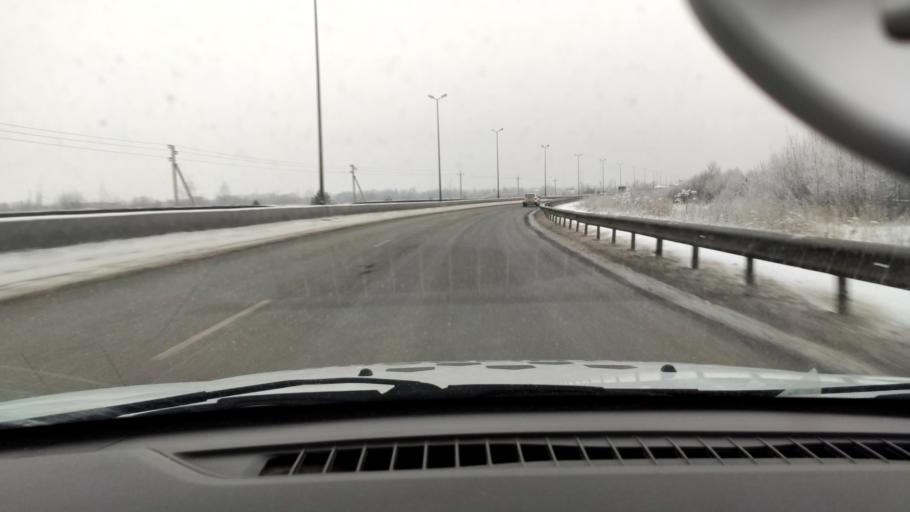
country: RU
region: Perm
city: Kondratovo
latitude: 58.0051
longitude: 56.0707
